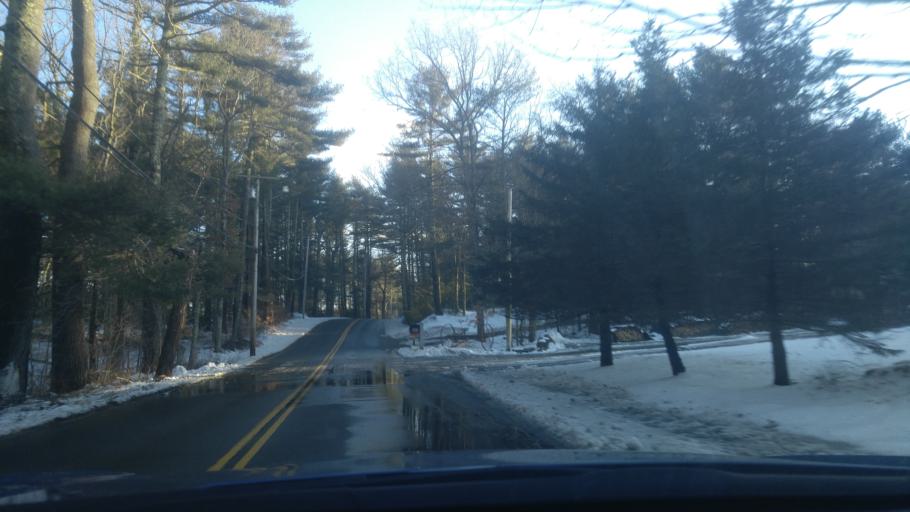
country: US
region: Rhode Island
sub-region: Kent County
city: Coventry
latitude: 41.7184
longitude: -71.6531
